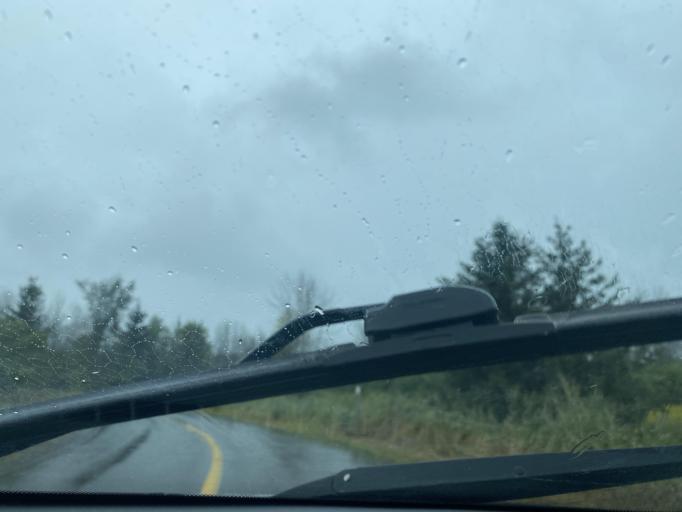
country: CA
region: Quebec
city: Baie-D'Urfe
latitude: 45.4656
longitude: -73.9230
